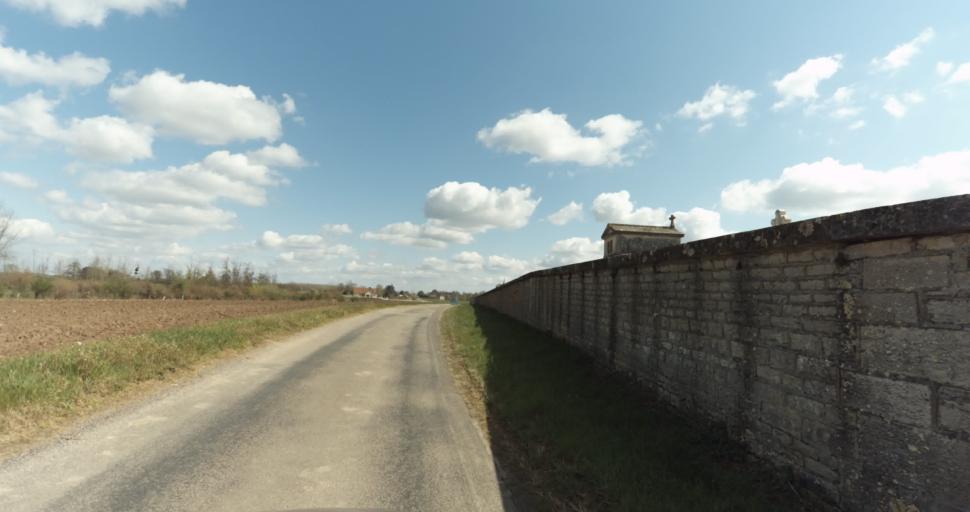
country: FR
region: Bourgogne
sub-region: Departement de la Cote-d'Or
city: Auxonne
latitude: 47.2024
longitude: 5.3982
